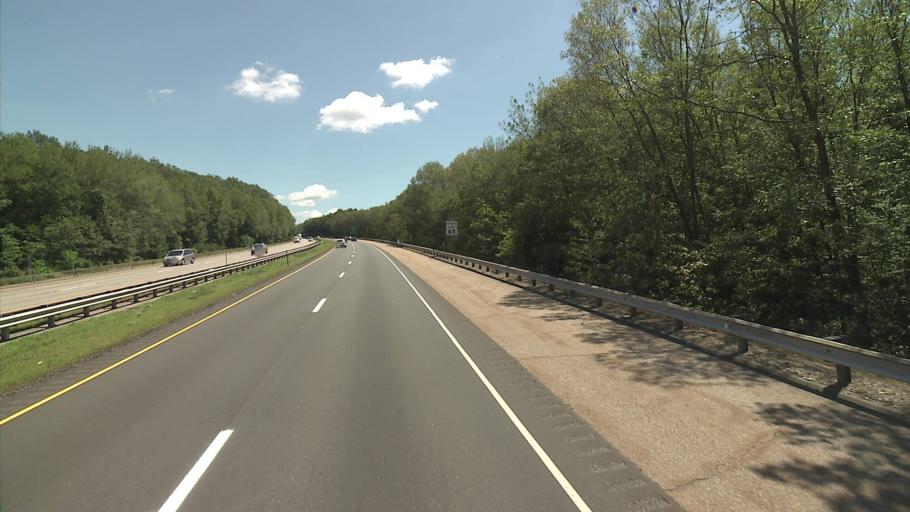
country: US
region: Connecticut
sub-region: New London County
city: Lisbon
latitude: 41.5854
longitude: -72.0386
